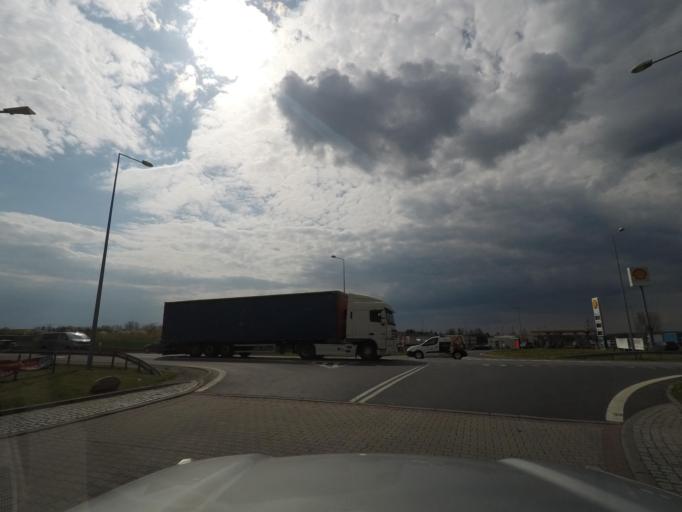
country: PL
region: Lower Silesian Voivodeship
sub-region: Legnica
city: Legnica
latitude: 51.1583
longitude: 16.1736
